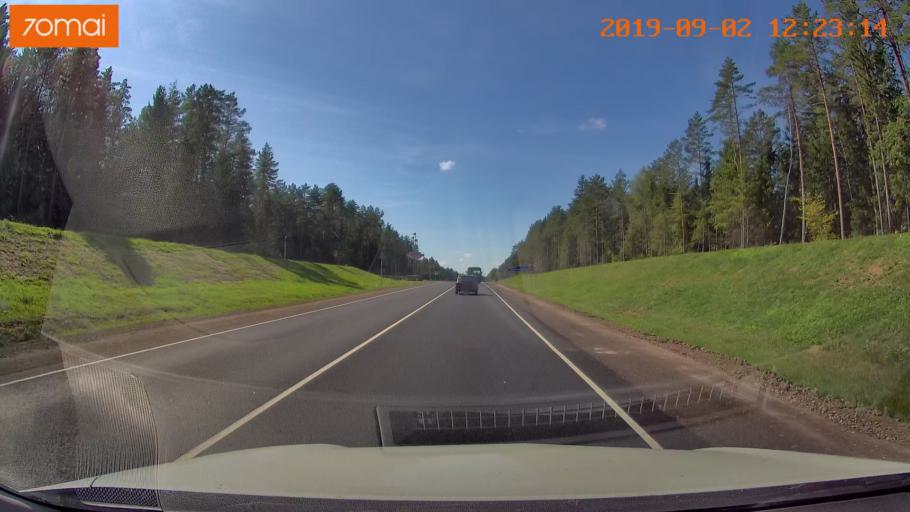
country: RU
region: Smolensk
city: Shumyachi
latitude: 53.8757
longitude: 32.6227
